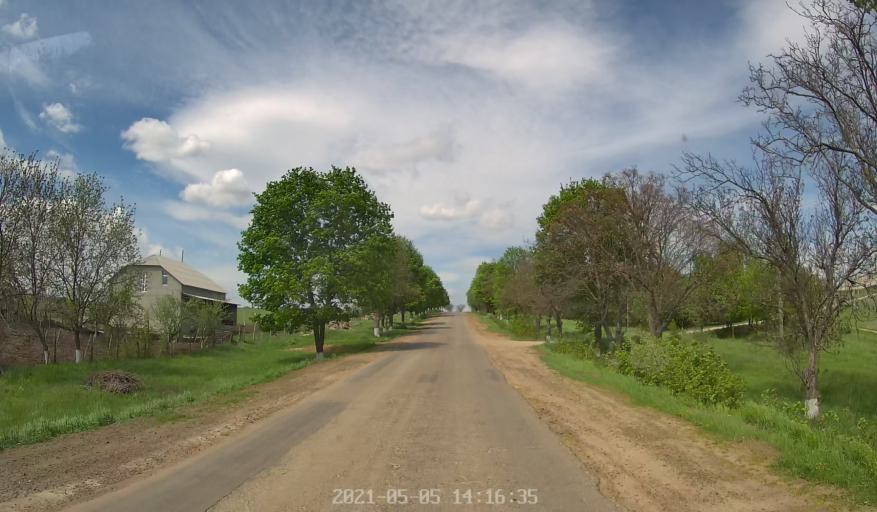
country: MD
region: Chisinau
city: Vadul lui Voda
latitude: 47.0745
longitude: 29.1365
